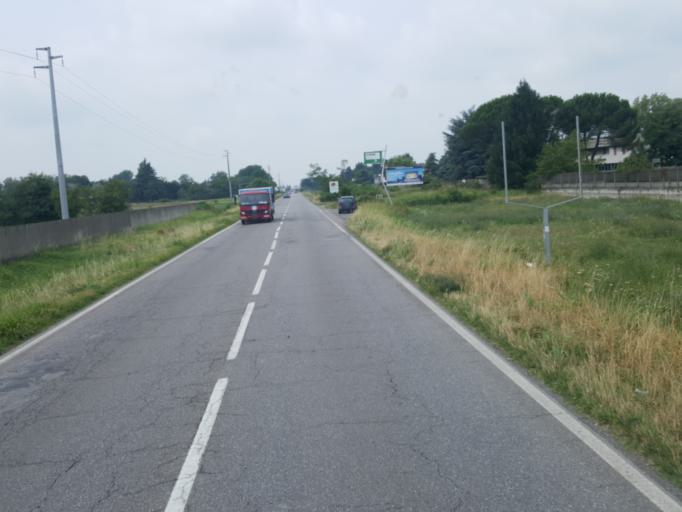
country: IT
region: Lombardy
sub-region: Provincia di Cremona
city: Vailate
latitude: 45.4771
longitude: 9.5989
